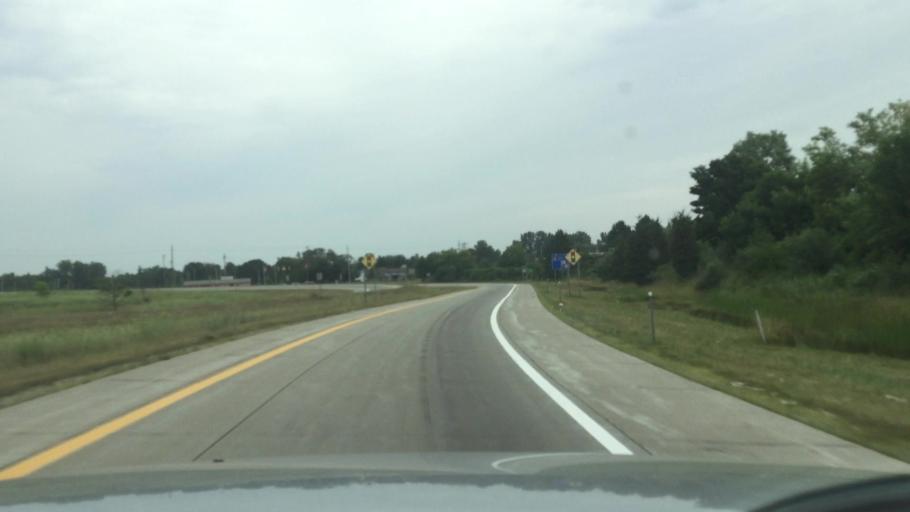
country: US
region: Michigan
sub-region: Genesee County
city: Grand Blanc
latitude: 42.9417
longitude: -83.6805
